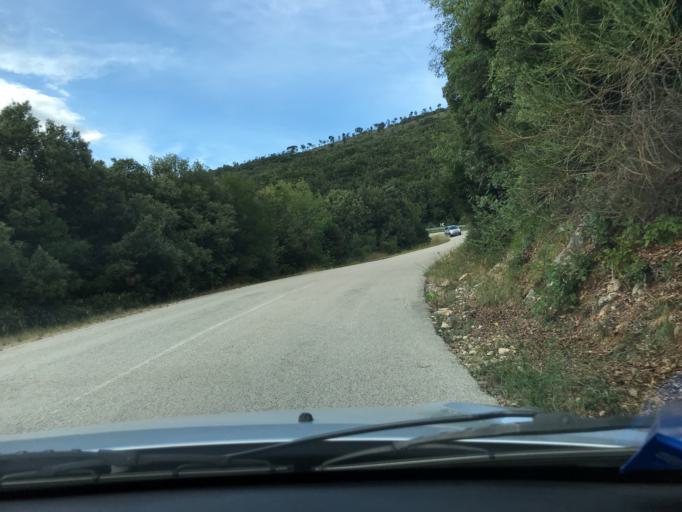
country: IT
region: Umbria
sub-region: Provincia di Terni
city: Montecchio
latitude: 42.6857
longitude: 12.2973
